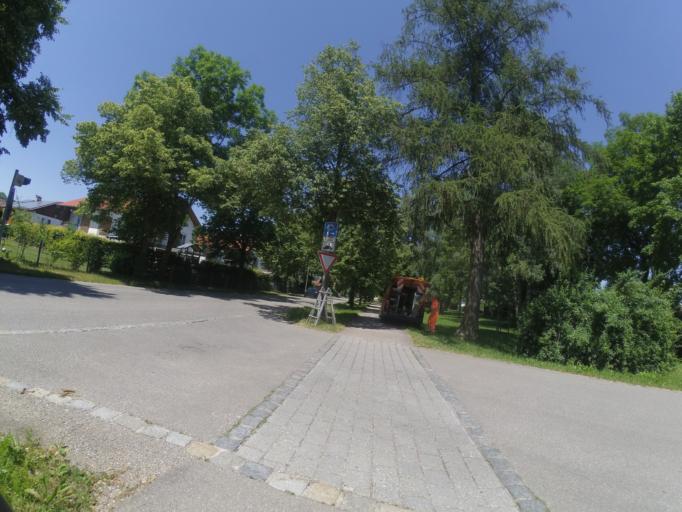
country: DE
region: Bavaria
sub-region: Swabia
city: Ottobeuren
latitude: 47.9365
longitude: 10.3038
